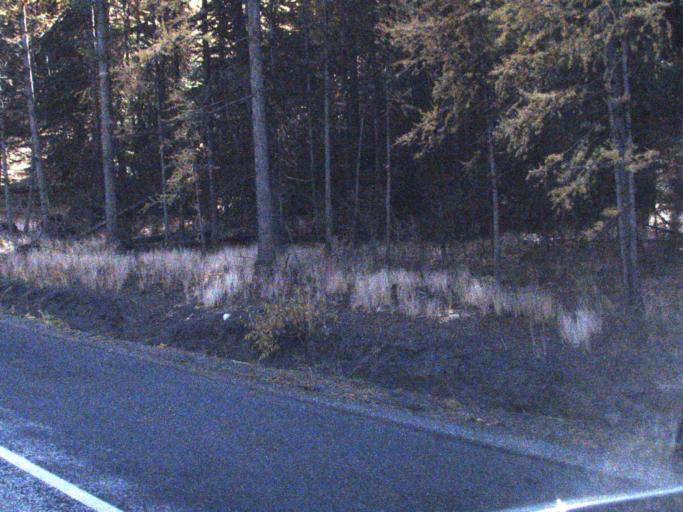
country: US
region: Washington
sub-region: Ferry County
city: Republic
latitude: 48.6115
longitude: -118.5446
